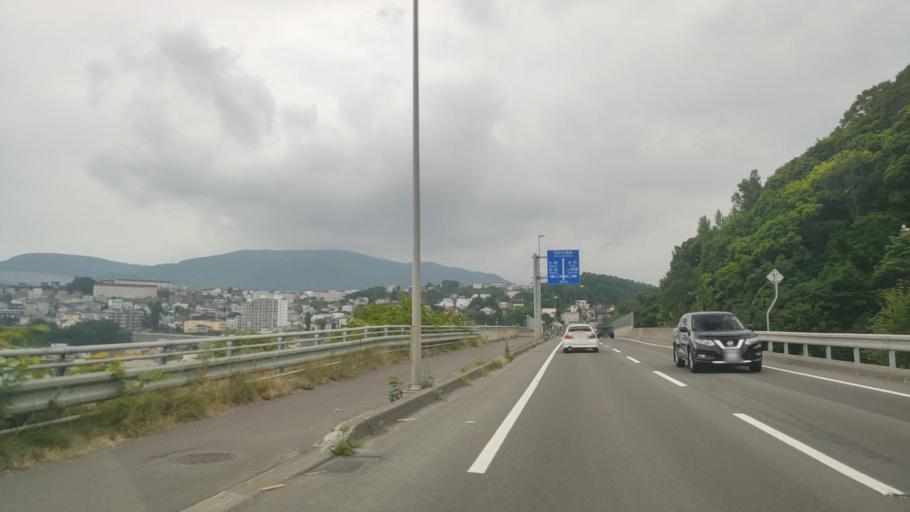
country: JP
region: Hokkaido
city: Otaru
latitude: 43.1813
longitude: 141.0369
